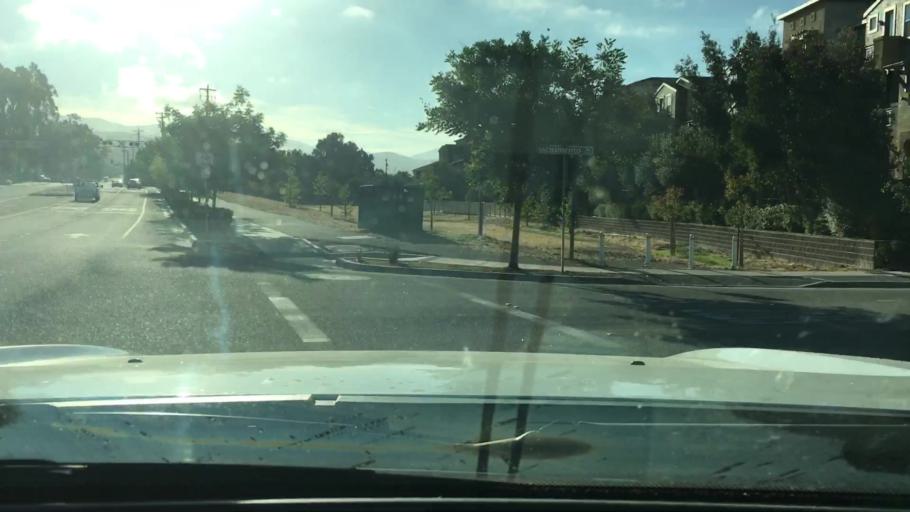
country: US
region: California
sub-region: San Luis Obispo County
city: San Luis Obispo
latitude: 35.2612
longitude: -120.6462
